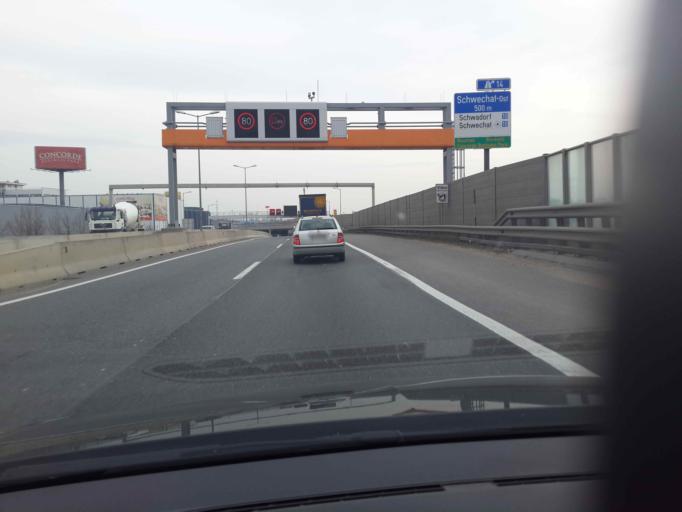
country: AT
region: Lower Austria
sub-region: Politischer Bezirk Wien-Umgebung
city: Schwechat
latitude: 48.1420
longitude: 16.4872
